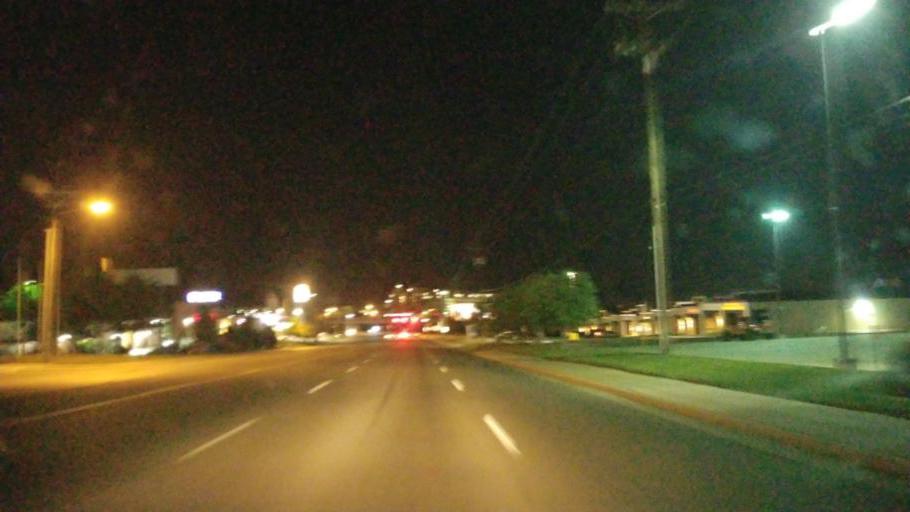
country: US
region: Texas
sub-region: Potter County
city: Amarillo
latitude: 35.1891
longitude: -101.9203
